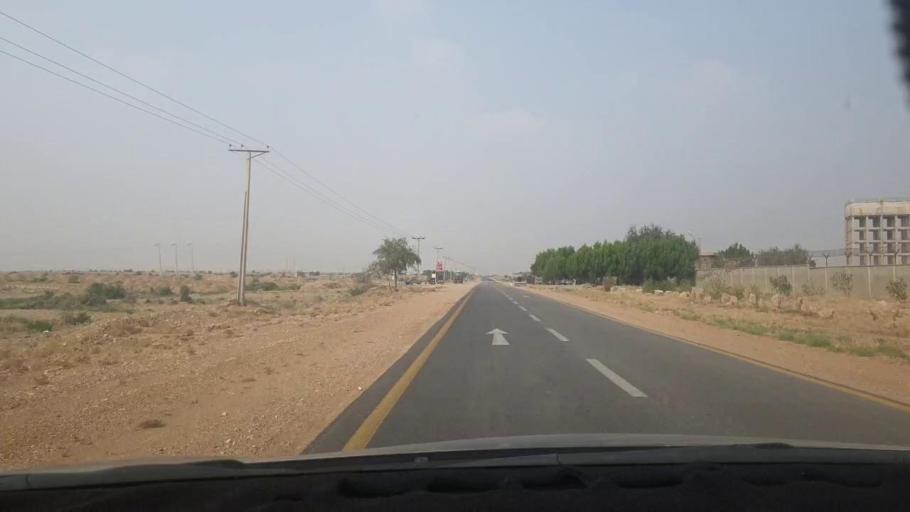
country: PK
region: Sindh
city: Jamshoro
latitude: 25.5594
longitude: 68.3188
